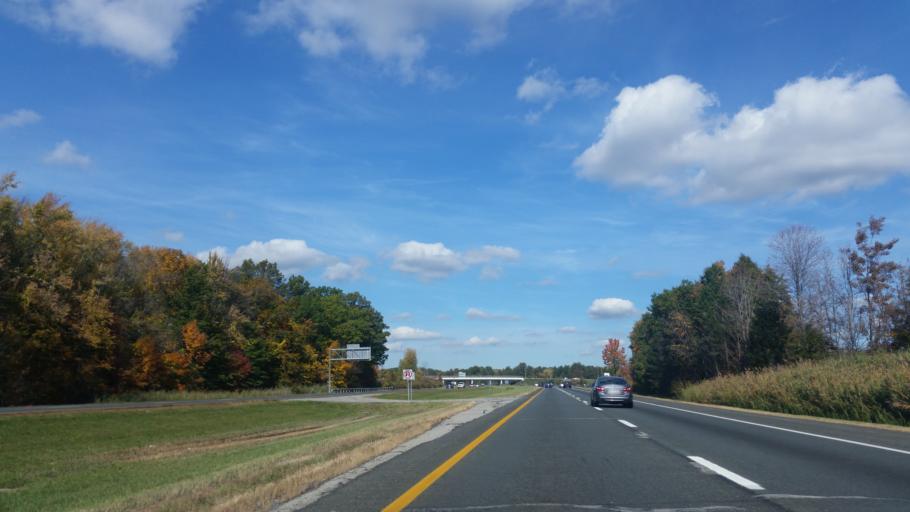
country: US
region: Ohio
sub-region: Cuyahoga County
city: Brecksville
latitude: 41.2833
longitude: -81.6361
